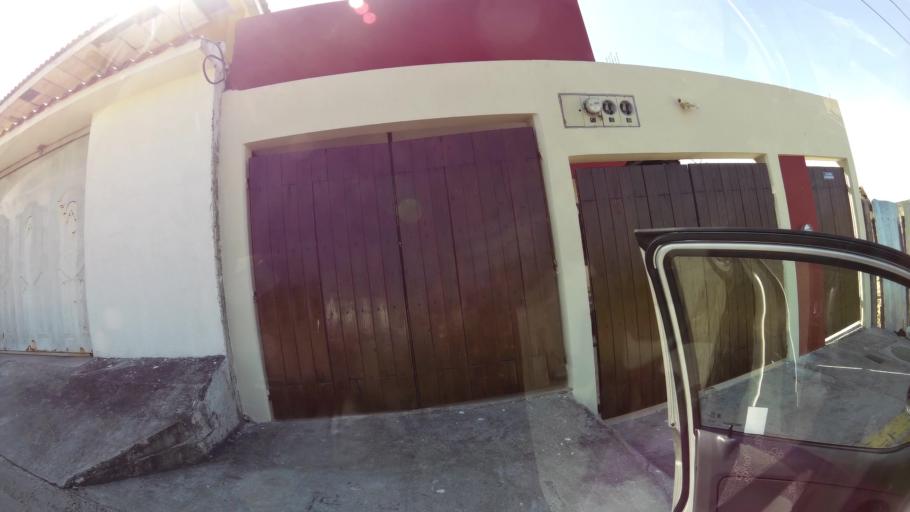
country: EC
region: Guayas
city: Guayaquil
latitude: -2.1844
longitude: -79.9178
